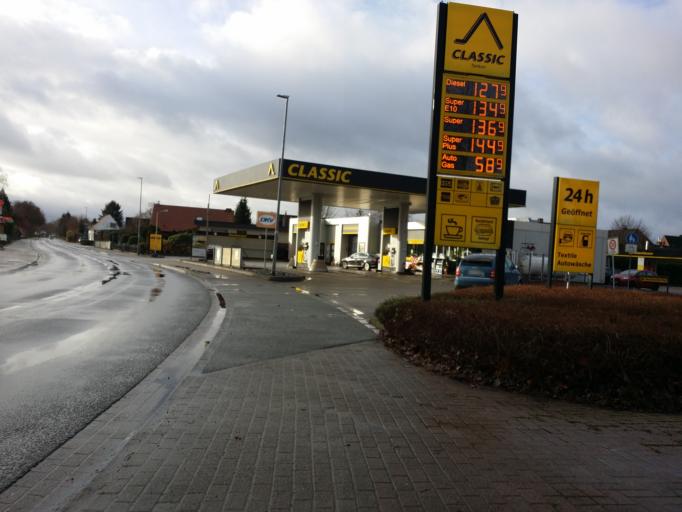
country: DE
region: Lower Saxony
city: Stuhr
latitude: 52.9911
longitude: 8.8064
